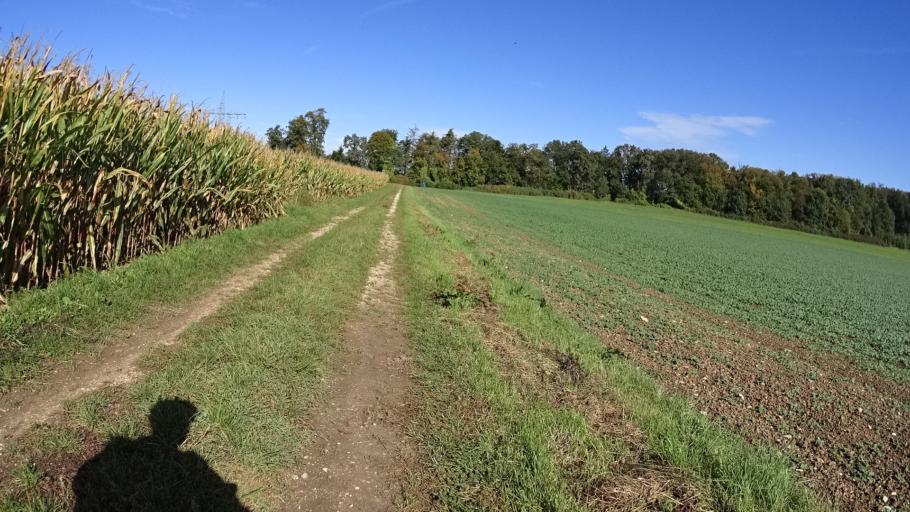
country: DE
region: Bavaria
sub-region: Upper Bavaria
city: Adelschlag
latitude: 48.8719
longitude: 11.2394
